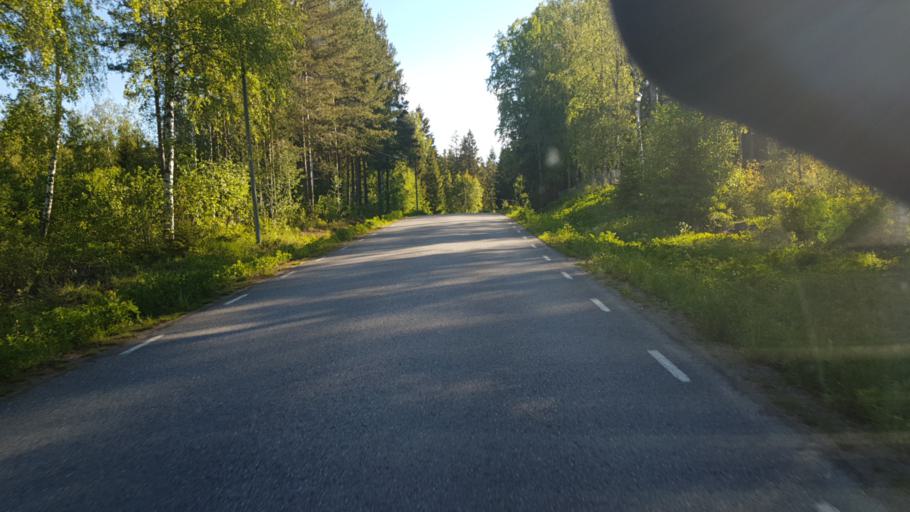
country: SE
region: Vaermland
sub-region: Arvika Kommun
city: Arvika
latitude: 59.5540
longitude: 12.4182
